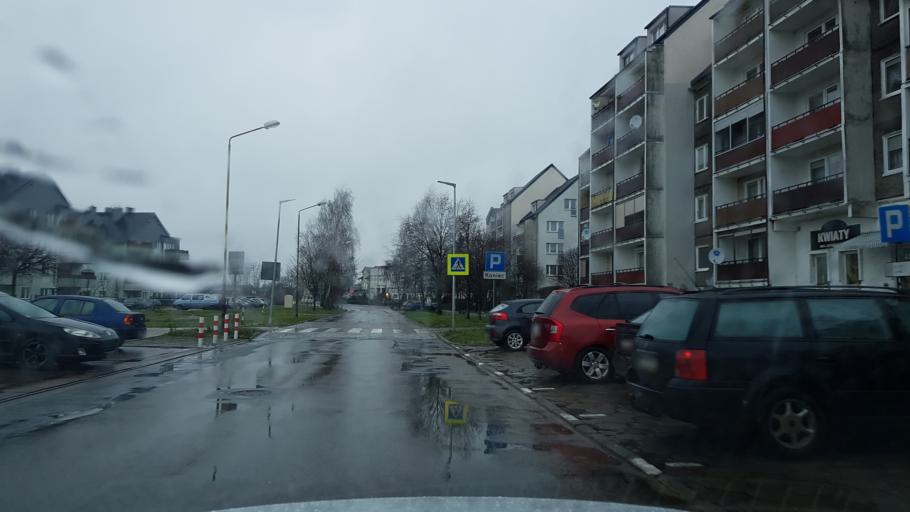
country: PL
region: West Pomeranian Voivodeship
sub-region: Powiat stargardzki
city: Stargard Szczecinski
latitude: 53.3149
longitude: 15.0348
